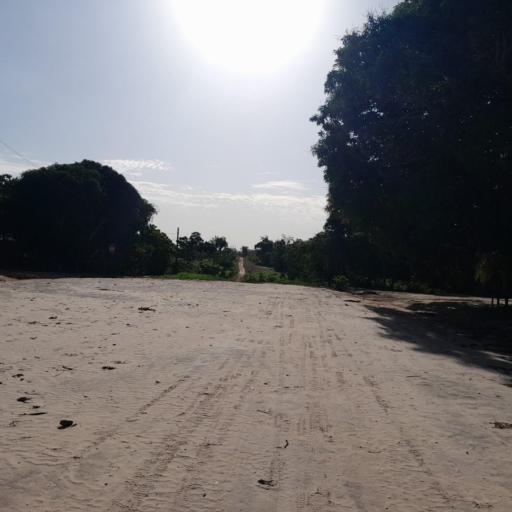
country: PE
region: Ucayali
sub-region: Provincia de Coronel Portillo
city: Puerto Callao
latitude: -8.2751
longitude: -74.6518
